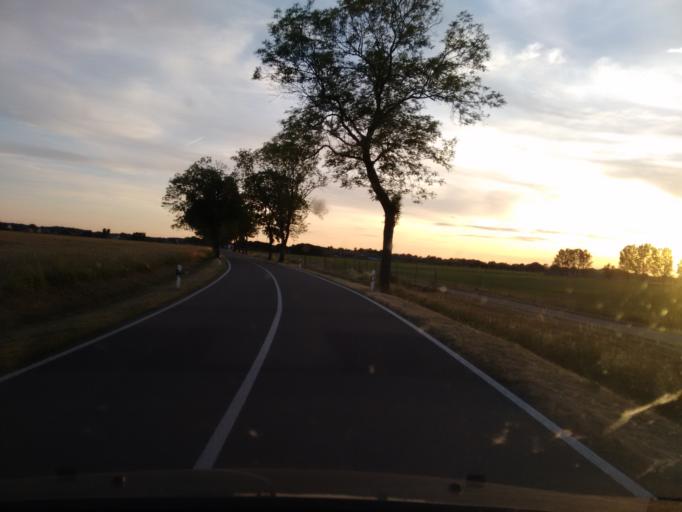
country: DE
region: Brandenburg
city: Mixdorf
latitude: 52.1697
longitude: 14.3421
